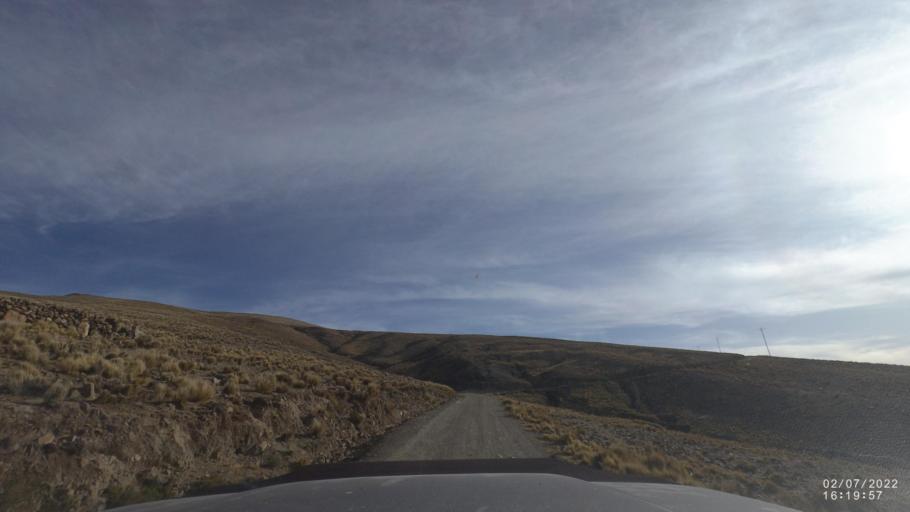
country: BO
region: Cochabamba
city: Irpa Irpa
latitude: -17.9308
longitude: -66.4456
